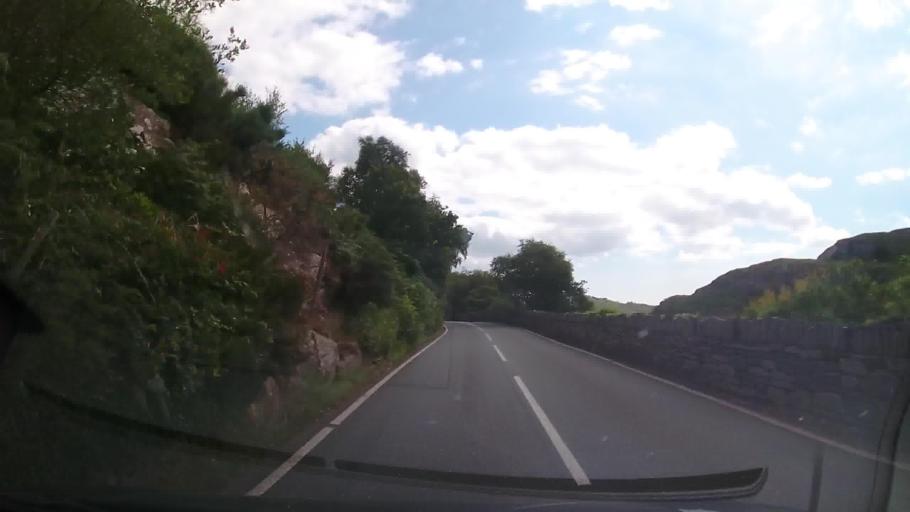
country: GB
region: Wales
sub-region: Gwynedd
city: Penrhyndeudraeth
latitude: 52.9335
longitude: -4.0404
